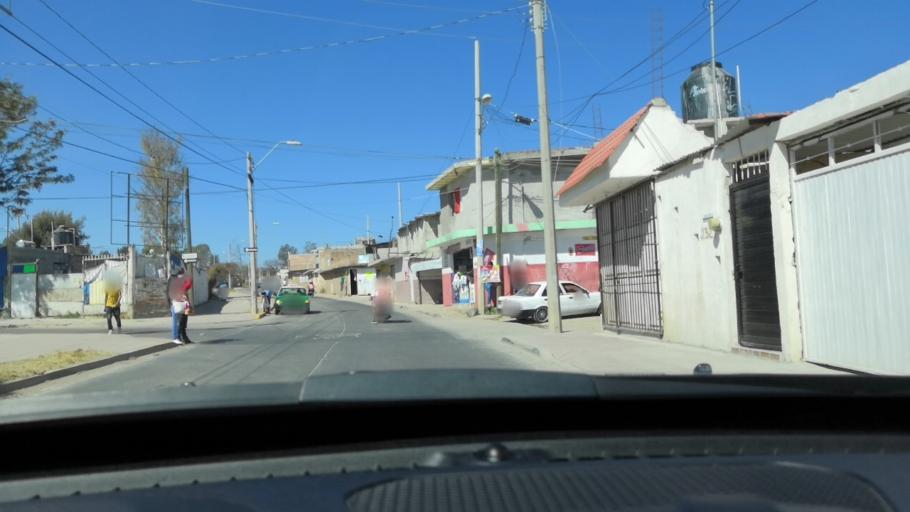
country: MX
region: Guanajuato
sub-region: Leon
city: Centro Familiar la Soledad
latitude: 21.1420
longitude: -101.7542
